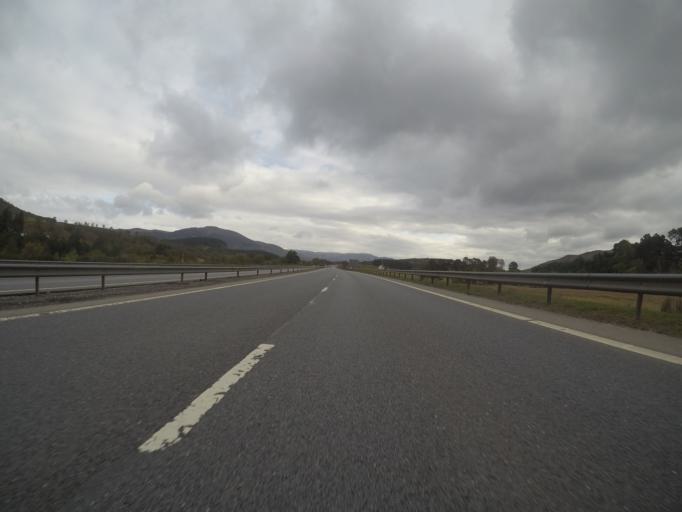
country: GB
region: Scotland
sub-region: Highland
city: Kingussie
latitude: 57.0042
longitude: -4.1691
